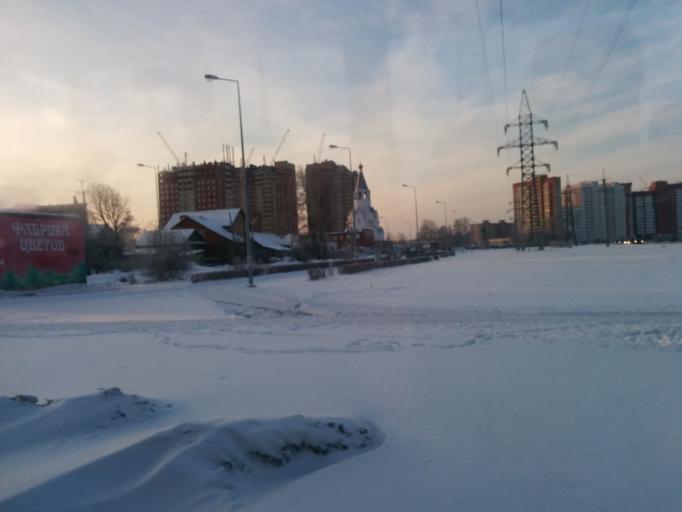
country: RU
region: Perm
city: Perm
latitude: 57.9899
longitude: 56.2977
